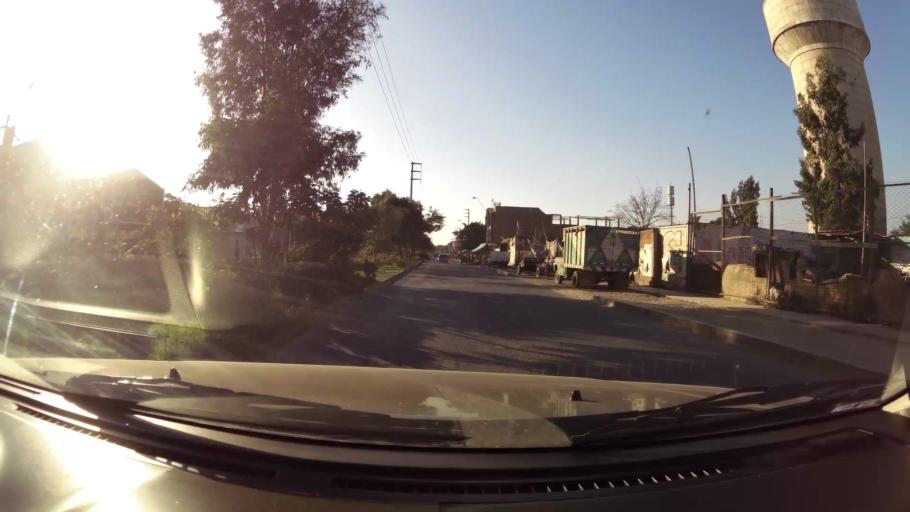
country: PE
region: Ica
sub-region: Provincia de Ica
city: Ica
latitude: -14.0641
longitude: -75.7204
